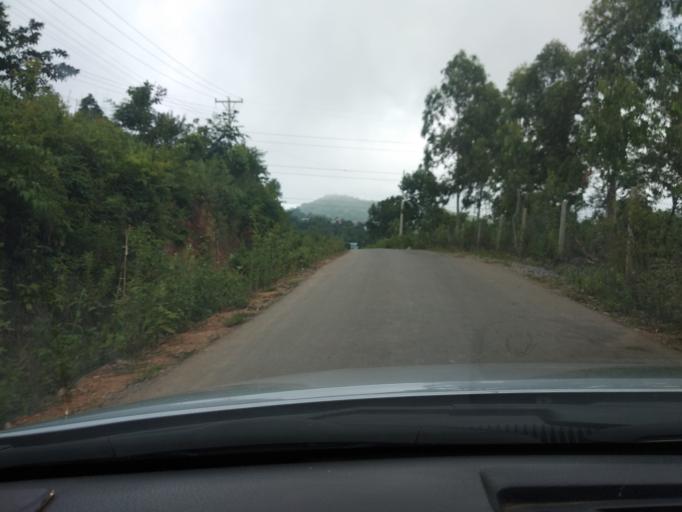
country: MM
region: Mandalay
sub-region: Pyin Oo Lwin District
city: Pyin Oo Lwin
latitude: 21.9128
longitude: 96.3829
